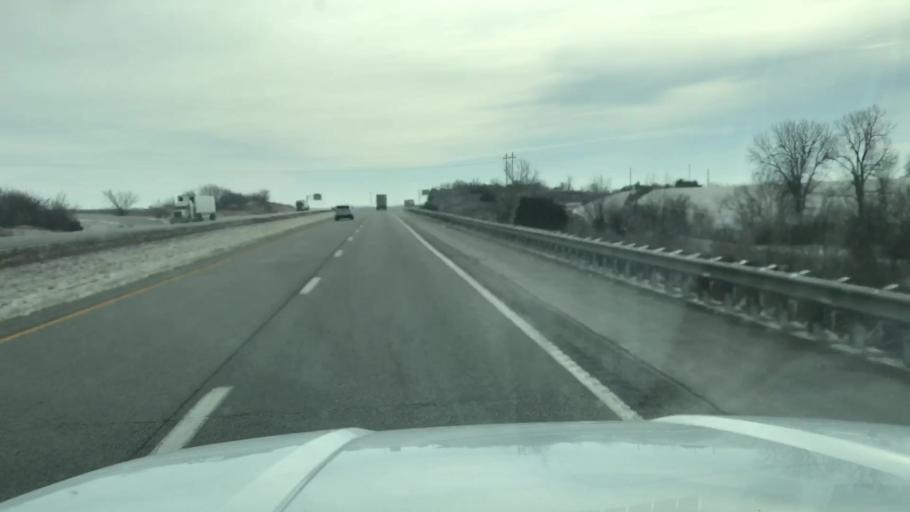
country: US
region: Missouri
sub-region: Andrew County
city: Savannah
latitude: 39.8907
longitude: -94.8638
